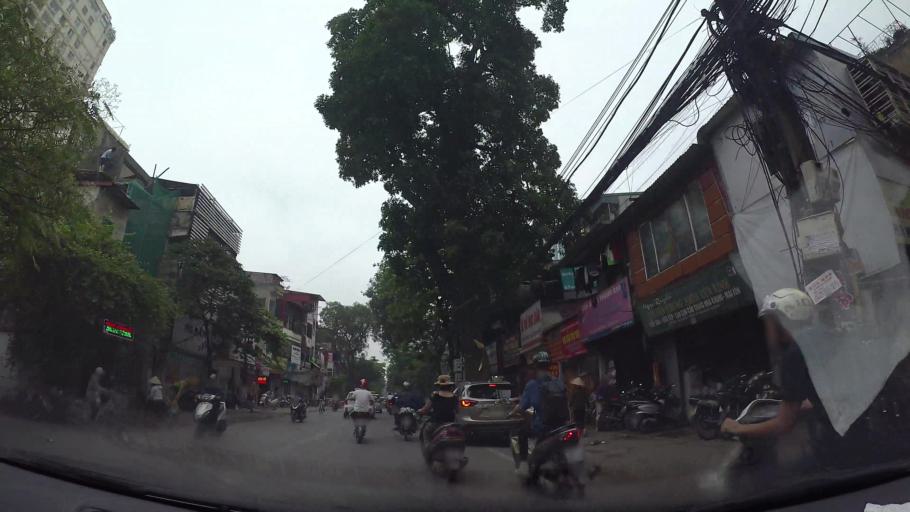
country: VN
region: Ha Noi
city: Hai BaTrung
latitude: 20.9956
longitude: 105.8529
